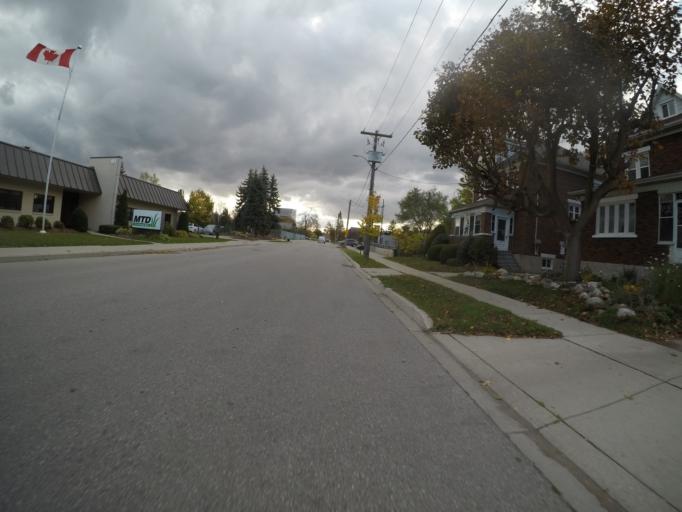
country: CA
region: Ontario
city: Kitchener
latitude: 43.4414
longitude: -80.4788
